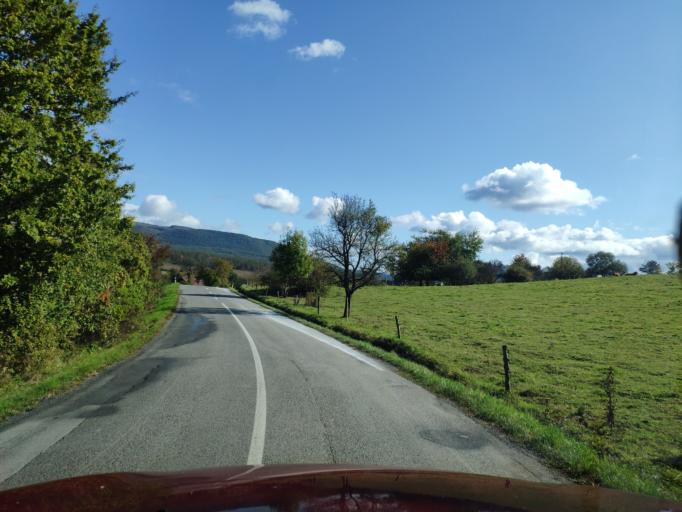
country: SK
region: Presovsky
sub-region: Okres Presov
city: Presov
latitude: 48.9504
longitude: 21.3023
